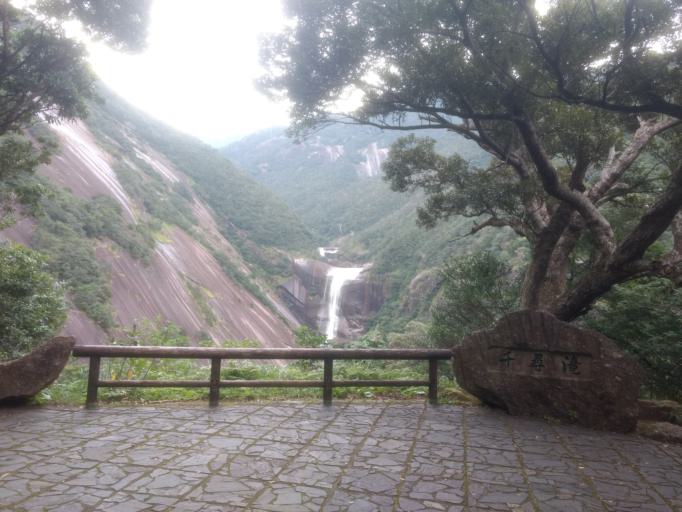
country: JP
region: Kagoshima
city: Nishinoomote
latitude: 30.2586
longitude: 130.5819
